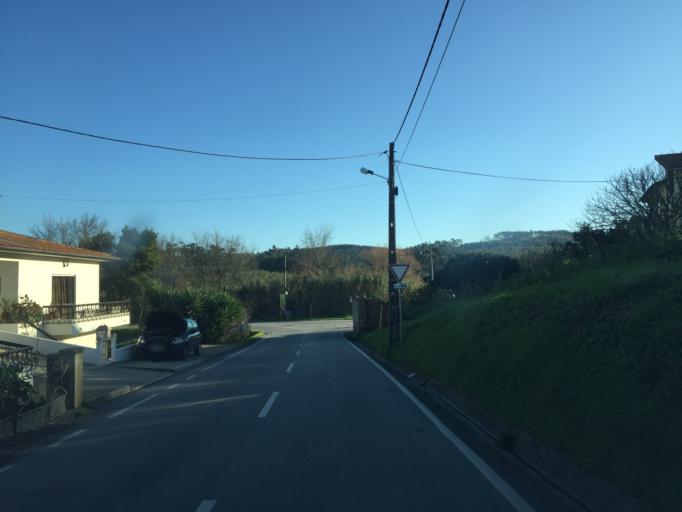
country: PT
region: Coimbra
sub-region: Figueira da Foz
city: Tavarede
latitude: 40.1629
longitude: -8.8177
